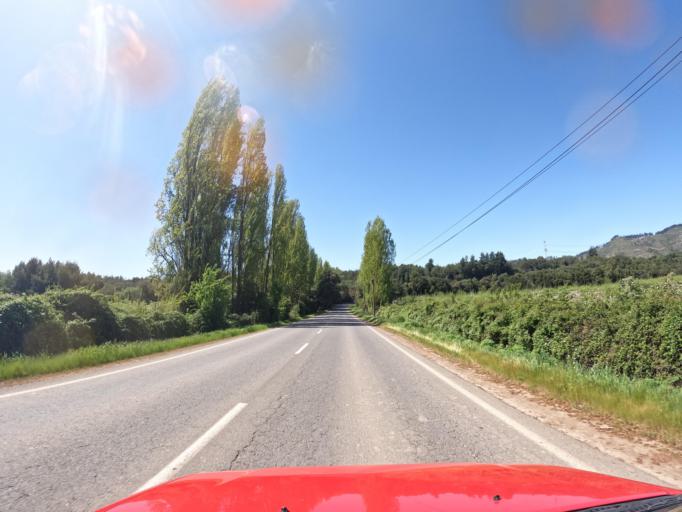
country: CL
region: Maule
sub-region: Provincia de Talca
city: San Clemente
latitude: -35.4877
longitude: -71.2928
